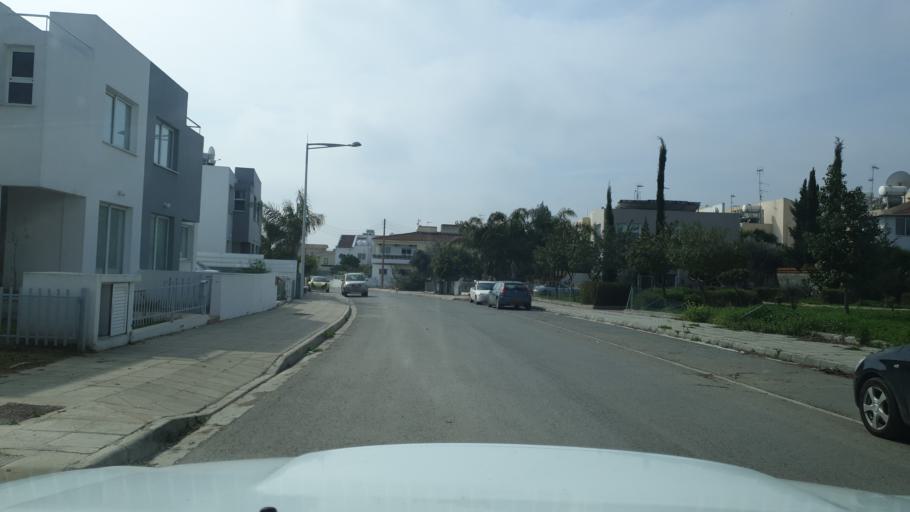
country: CY
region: Lefkosia
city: Tseri
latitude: 35.1213
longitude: 33.3503
